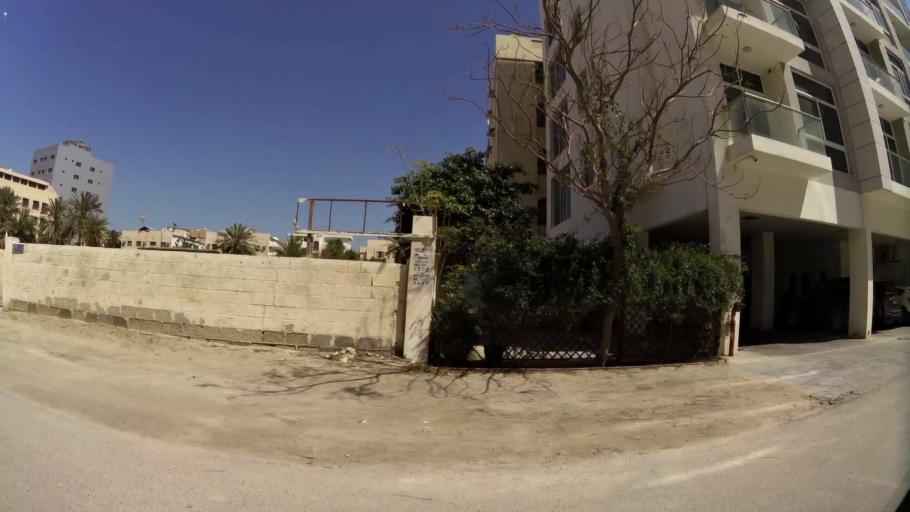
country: BH
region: Manama
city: Manama
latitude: 26.2030
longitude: 50.5987
